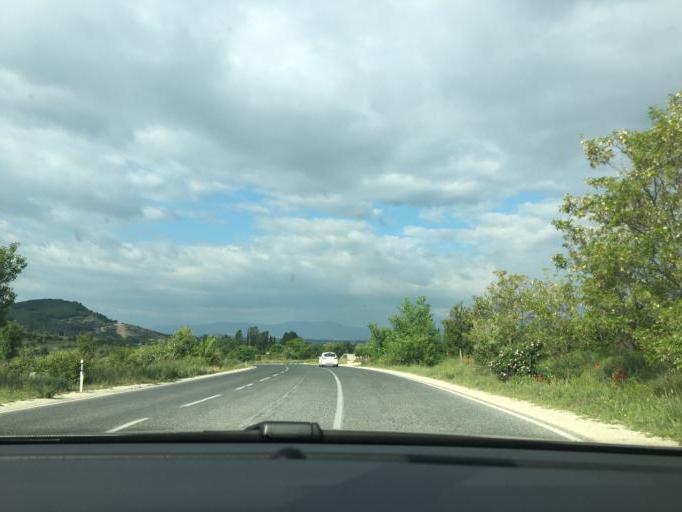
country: MK
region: Prilep
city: Prilep
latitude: 41.3681
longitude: 21.6114
